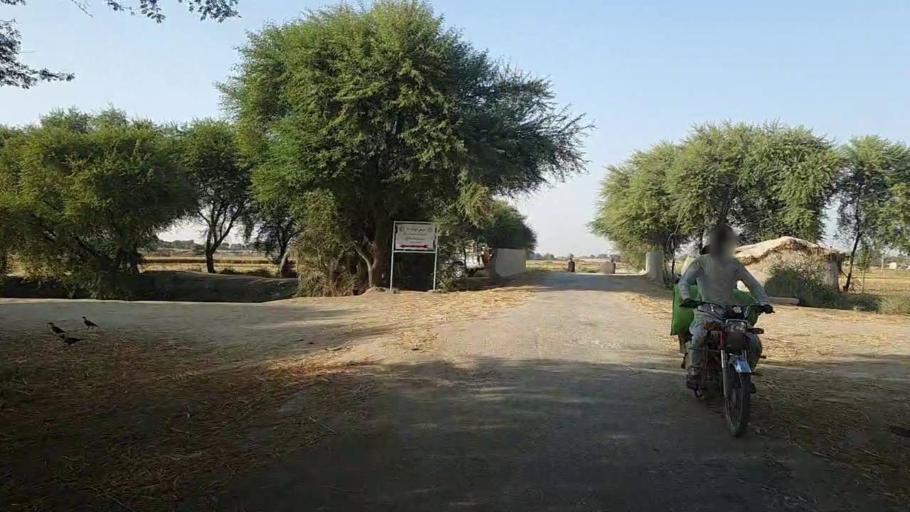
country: PK
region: Sindh
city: Kashmor
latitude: 28.4228
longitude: 69.4075
